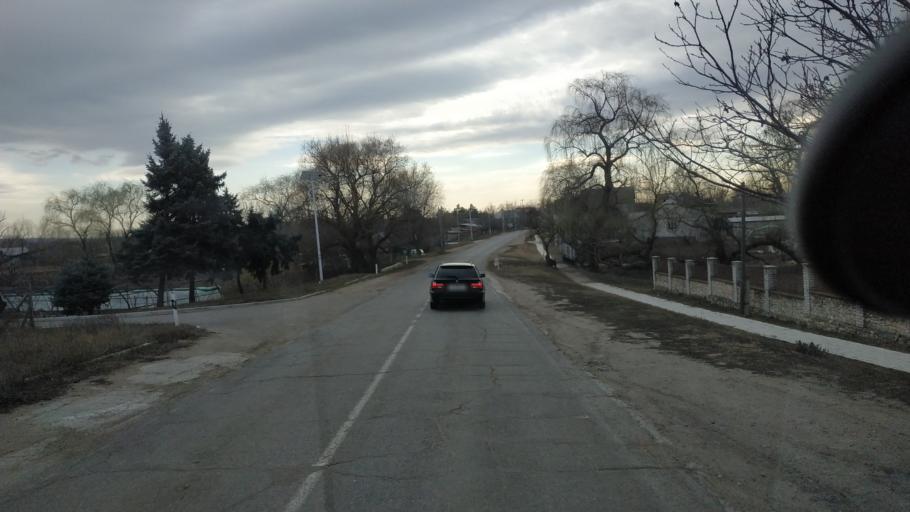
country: MD
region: Criuleni
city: Criuleni
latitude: 47.1637
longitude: 29.1205
